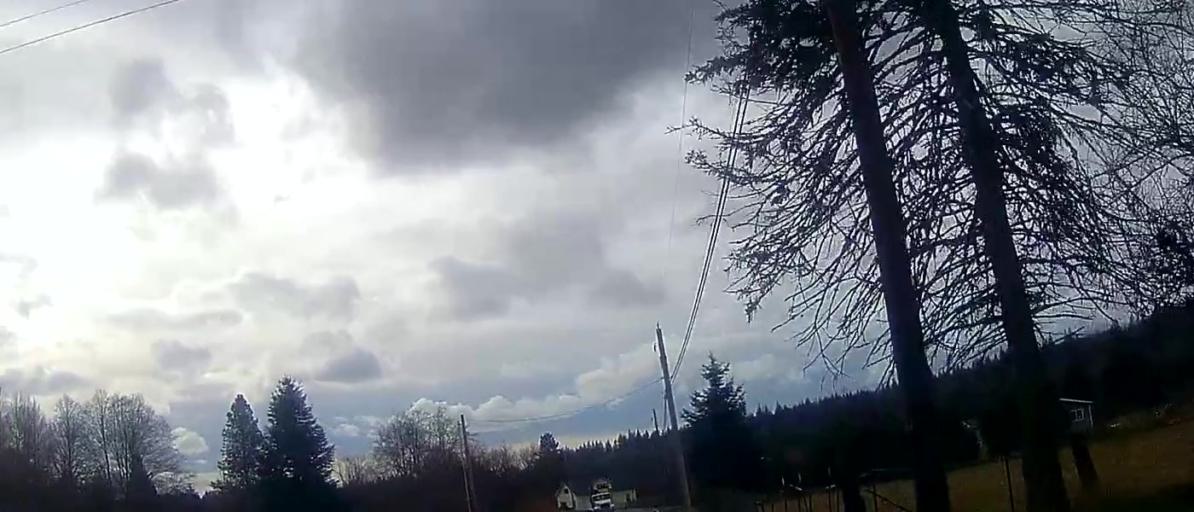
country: US
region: Washington
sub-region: Skagit County
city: Sedro-Woolley
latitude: 48.5769
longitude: -122.2966
